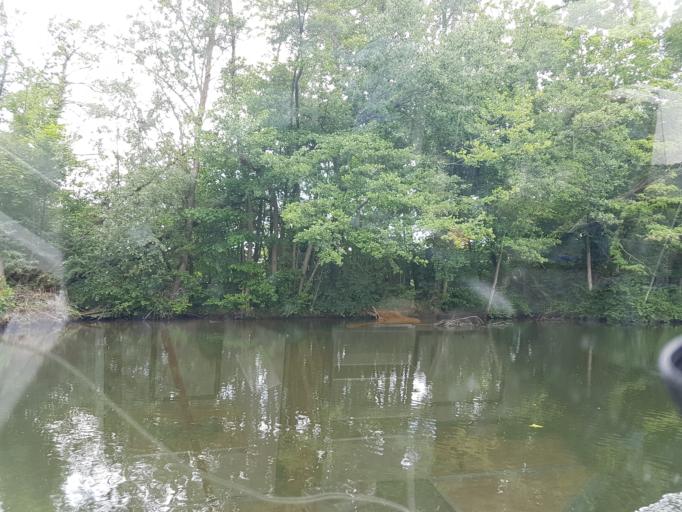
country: FR
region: Bourgogne
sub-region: Departement de l'Yonne
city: Moneteau
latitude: 47.8505
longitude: 3.5769
